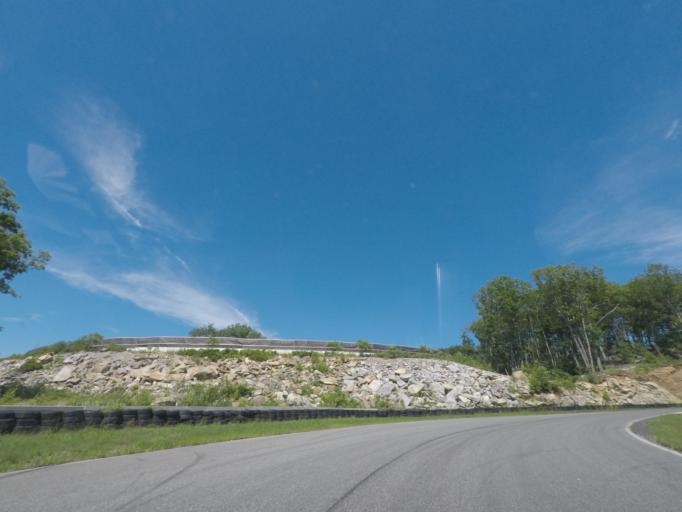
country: US
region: Massachusetts
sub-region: Hampshire County
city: Ware
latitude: 42.2357
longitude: -72.2443
